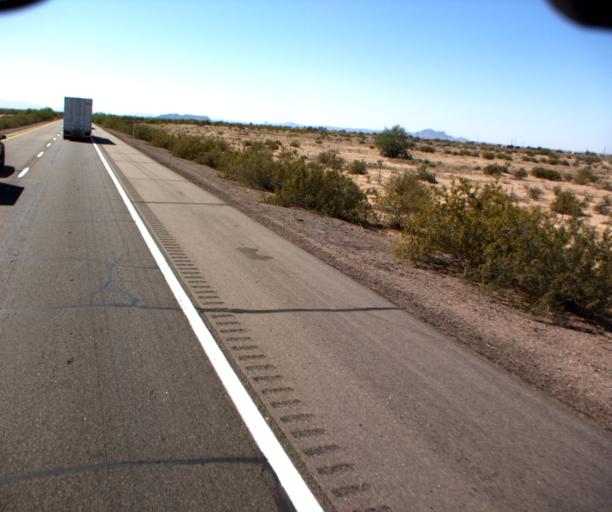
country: US
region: Arizona
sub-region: Yuma County
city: Wellton
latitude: 32.7077
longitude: -113.8610
